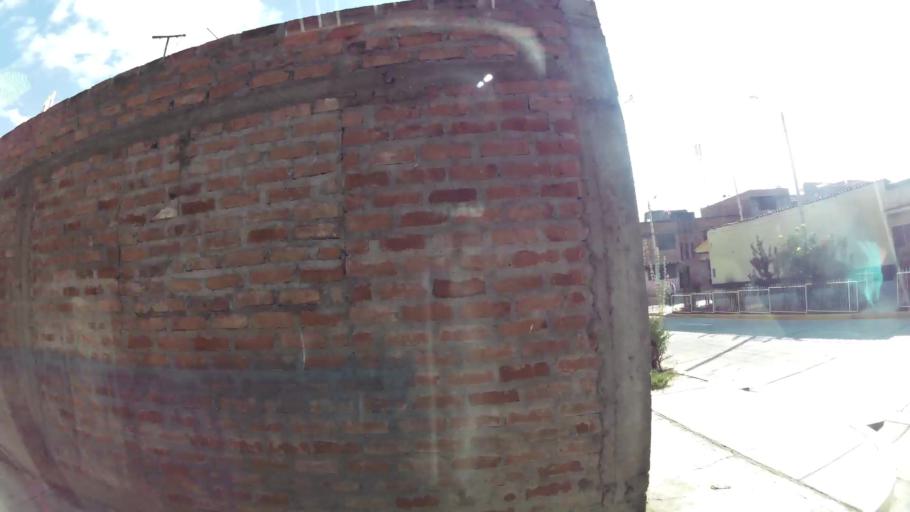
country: PE
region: Junin
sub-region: Provincia de Huancayo
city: El Tambo
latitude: -12.0603
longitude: -75.2270
